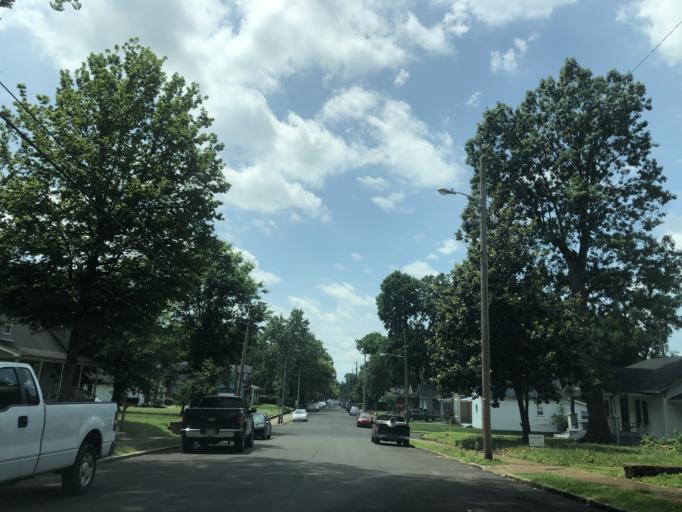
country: US
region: Tennessee
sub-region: Davidson County
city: Nashville
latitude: 36.1911
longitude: -86.7623
